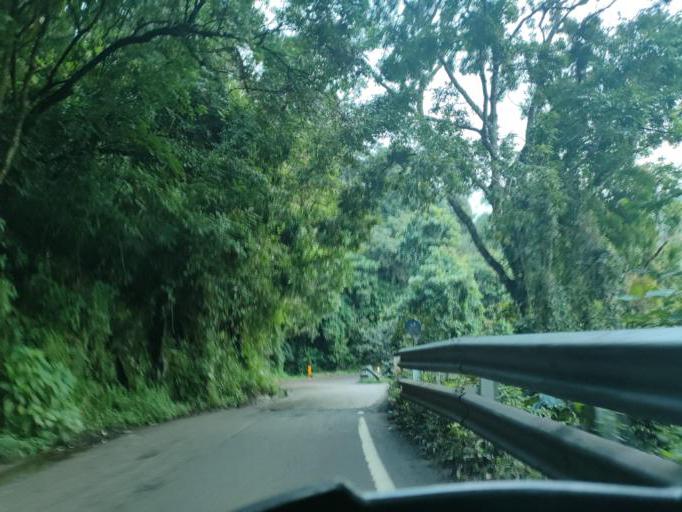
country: IN
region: Tamil Nadu
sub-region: Dindigul
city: Kodaikanal
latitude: 10.2547
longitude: 77.5275
